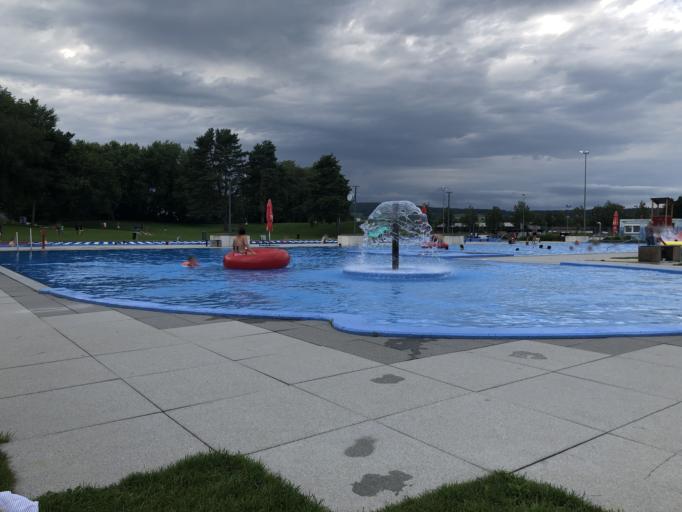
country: CH
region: Zurich
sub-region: Bezirk Dielsdorf
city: Dielsdorf
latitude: 47.4810
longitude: 8.4712
